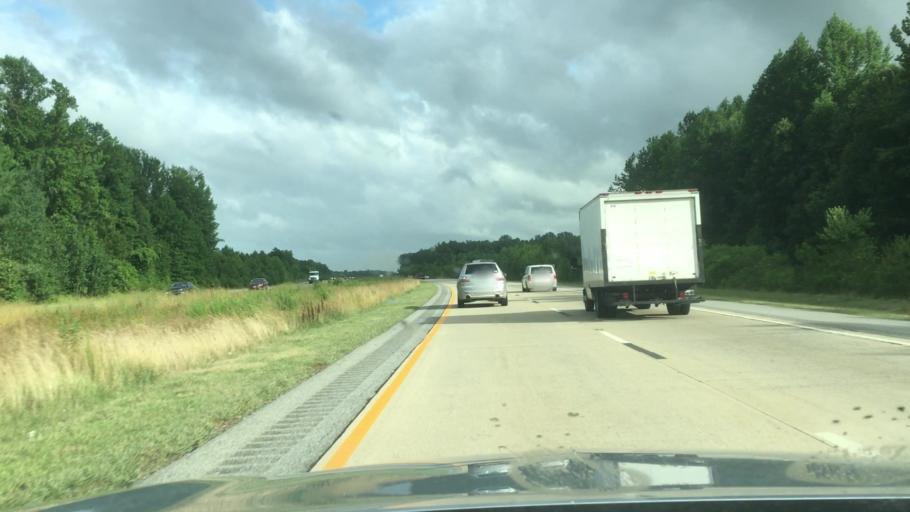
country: US
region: Delaware
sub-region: New Castle County
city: Townsend
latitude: 39.3587
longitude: -75.6527
